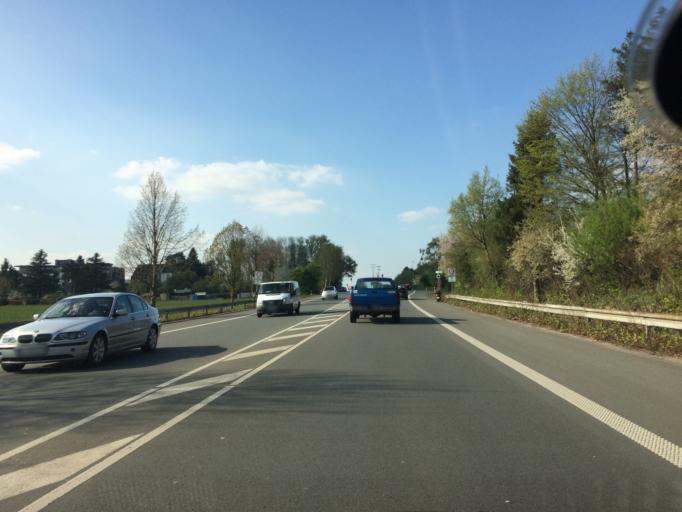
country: DE
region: North Rhine-Westphalia
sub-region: Regierungsbezirk Munster
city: Gelsenkirchen
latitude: 51.4559
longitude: 7.1390
